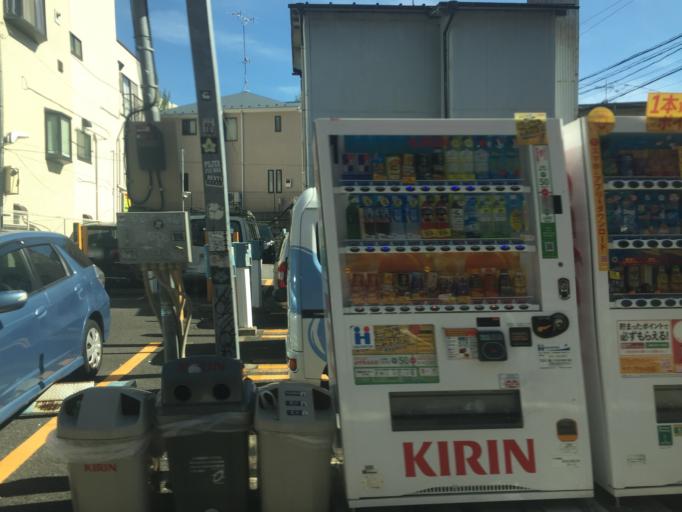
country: JP
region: Tokyo
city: Tokyo
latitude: 35.6535
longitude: 139.6989
